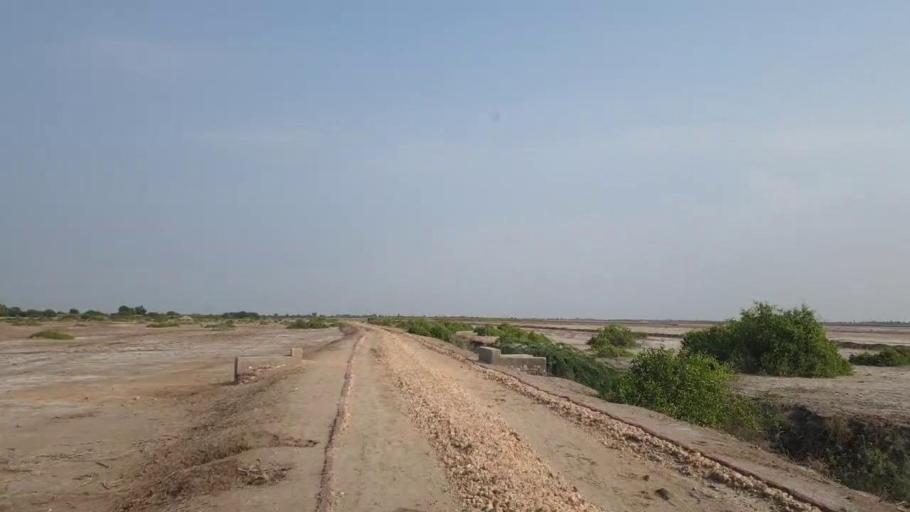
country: PK
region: Sindh
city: Kadhan
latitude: 24.4443
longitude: 68.8122
